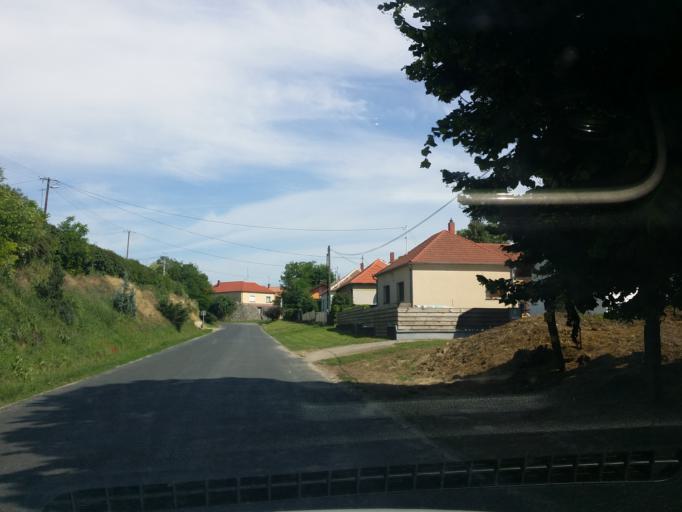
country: HU
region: Zala
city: Zalaszentgrot
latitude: 46.8865
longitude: 17.0736
